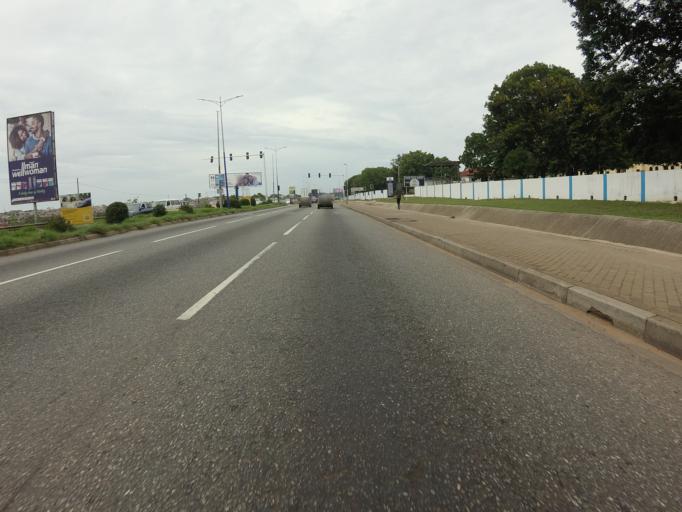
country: GH
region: Greater Accra
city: Accra
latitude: 5.5942
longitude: -0.2212
